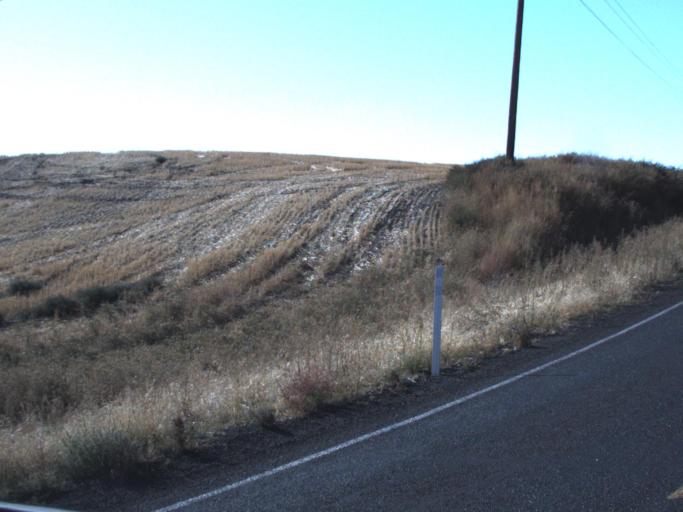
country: US
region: Washington
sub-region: Walla Walla County
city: Walla Walla
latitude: 46.1533
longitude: -118.3735
